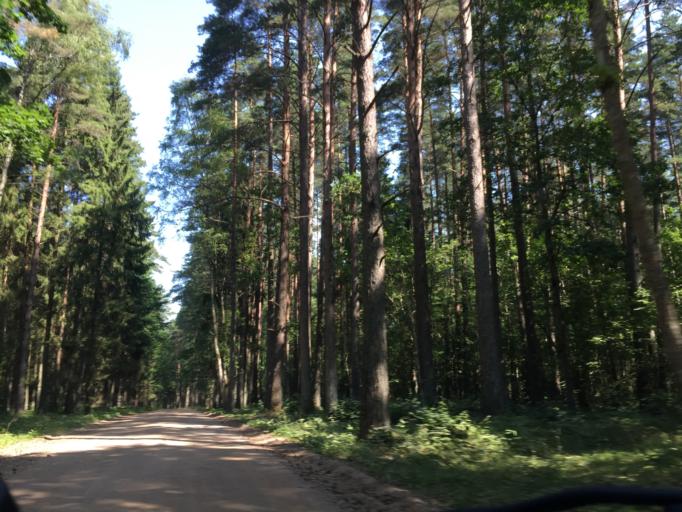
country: LV
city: Tervete
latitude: 56.4866
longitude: 23.4009
